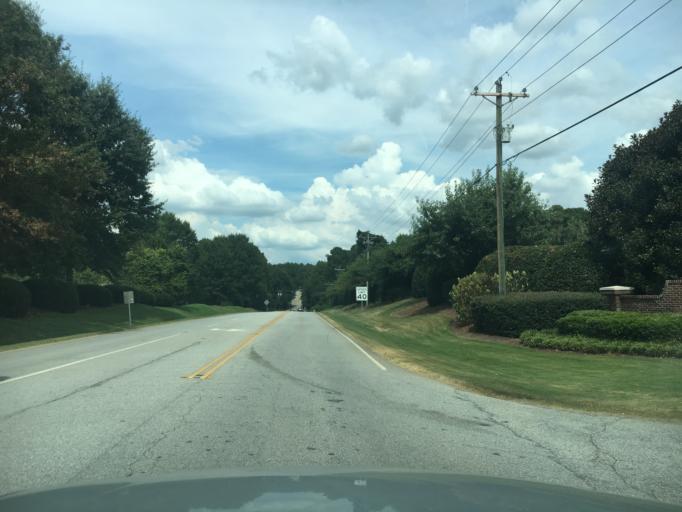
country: US
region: South Carolina
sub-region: Greenville County
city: Five Forks
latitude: 34.8127
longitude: -82.2322
